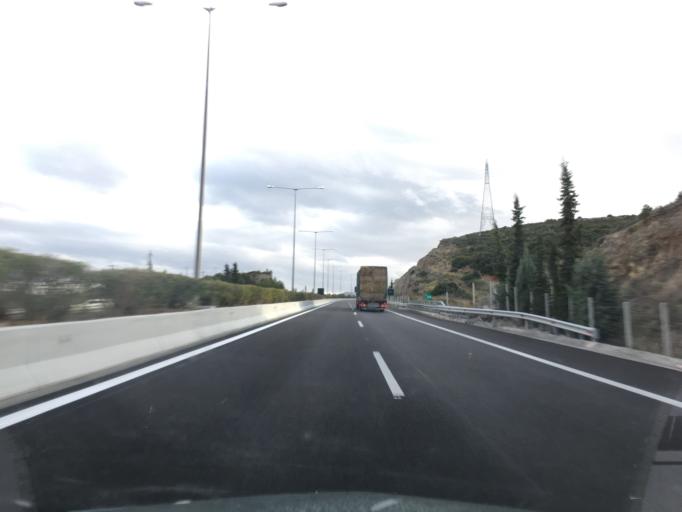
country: GR
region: Central Greece
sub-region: Nomos Fthiotidos
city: Pelasgia
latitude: 38.8980
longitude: 22.8366
